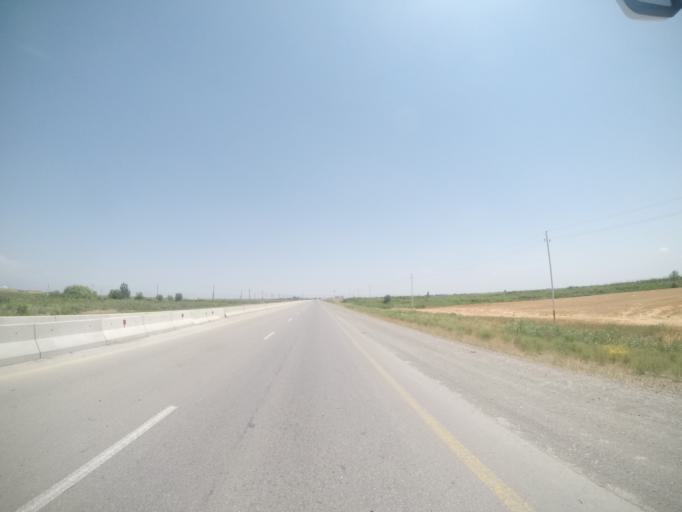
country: AZ
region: Kurdamir Rayon
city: Kyurdarmir
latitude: 40.3160
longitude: 48.1733
